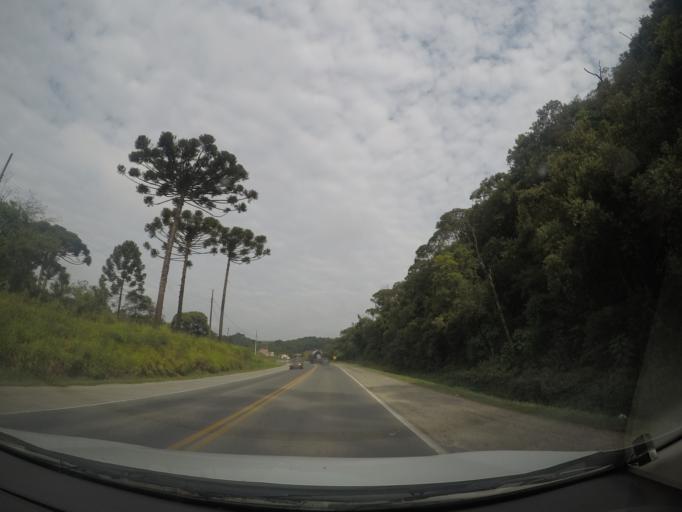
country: BR
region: Parana
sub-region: Almirante Tamandare
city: Almirante Tamandare
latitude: -25.3395
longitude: -49.2602
